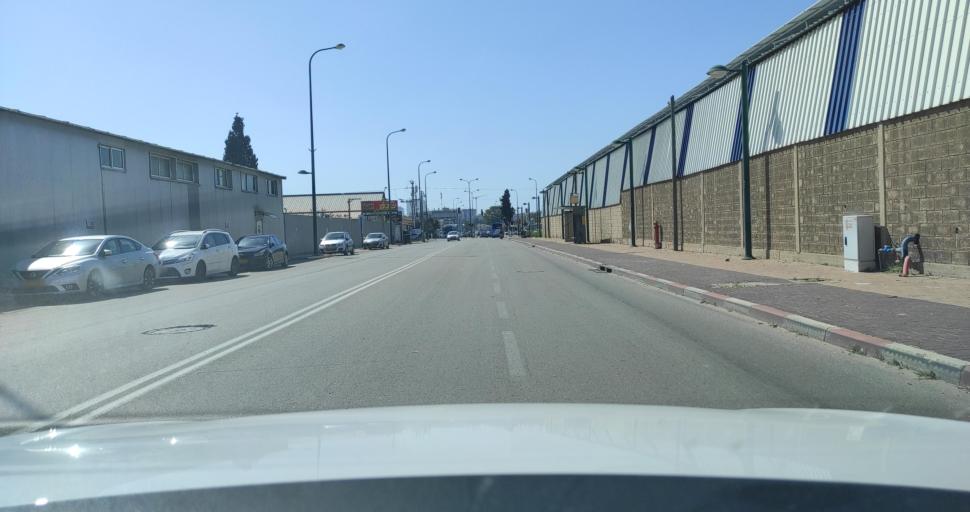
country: IL
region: Central District
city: Bet Yizhaq
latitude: 32.3199
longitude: 34.8798
